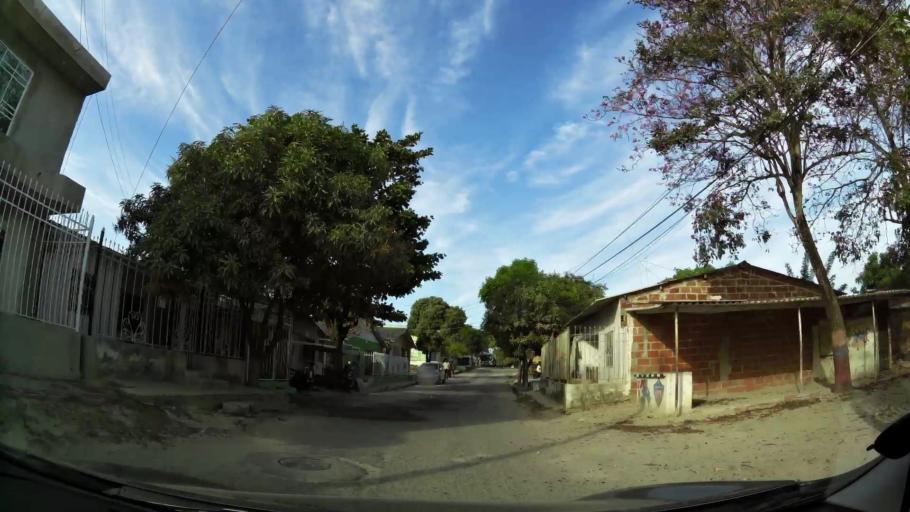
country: CO
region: Atlantico
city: Barranquilla
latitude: 10.9418
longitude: -74.8221
